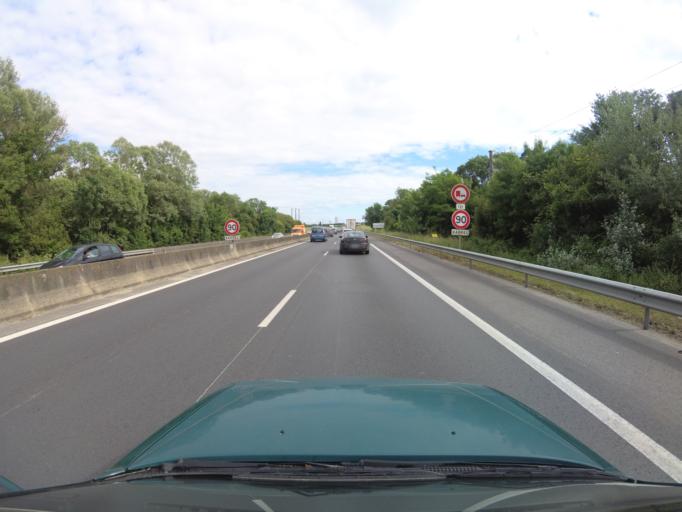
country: FR
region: Poitou-Charentes
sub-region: Departement de la Charente-Maritime
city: Aytre
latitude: 46.1492
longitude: -1.1114
